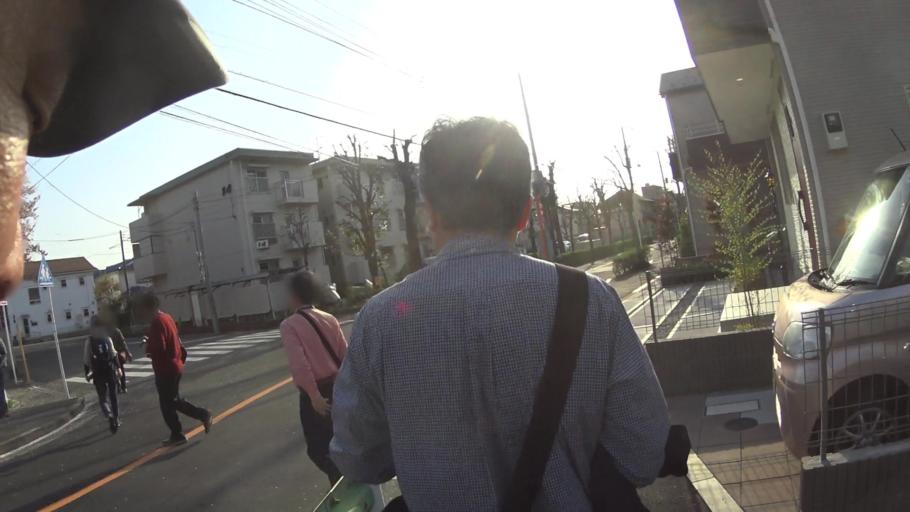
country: JP
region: Tokyo
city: Kokubunji
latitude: 35.7105
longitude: 139.5023
